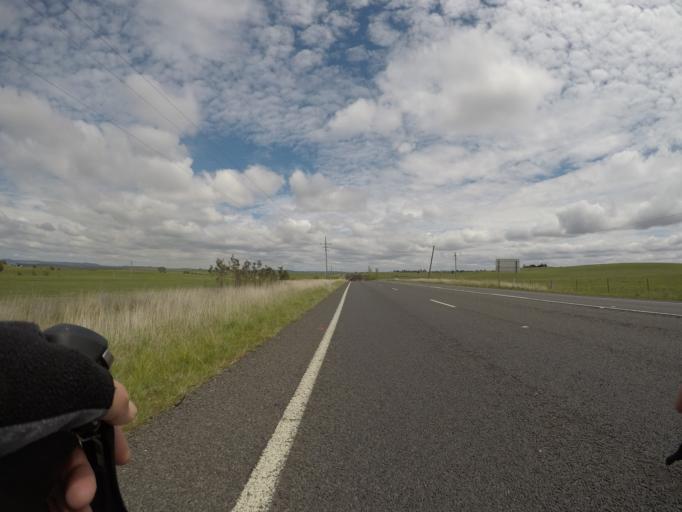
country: AU
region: New South Wales
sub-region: Bathurst Regional
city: Kelso
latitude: -33.4259
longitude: 149.6877
